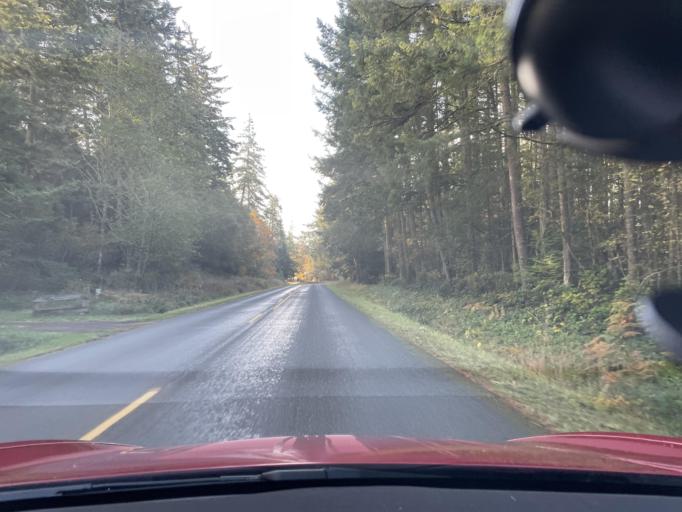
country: US
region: Washington
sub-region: San Juan County
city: Friday Harbor
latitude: 48.5532
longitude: -123.1646
